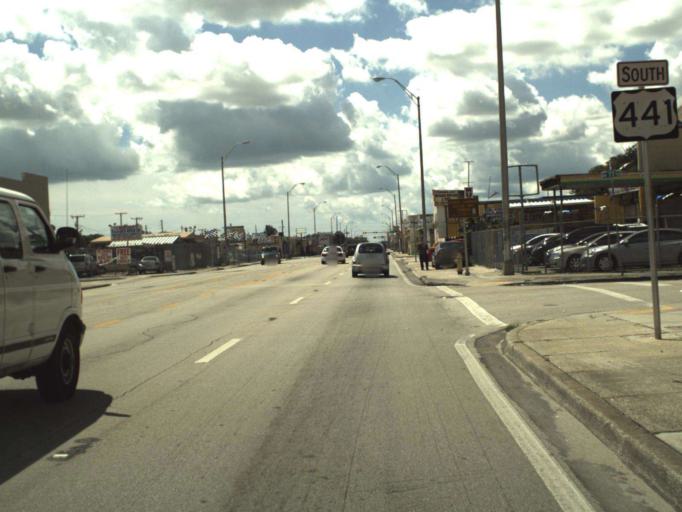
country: US
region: Florida
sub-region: Miami-Dade County
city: El Portal
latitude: 25.8458
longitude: -80.2092
